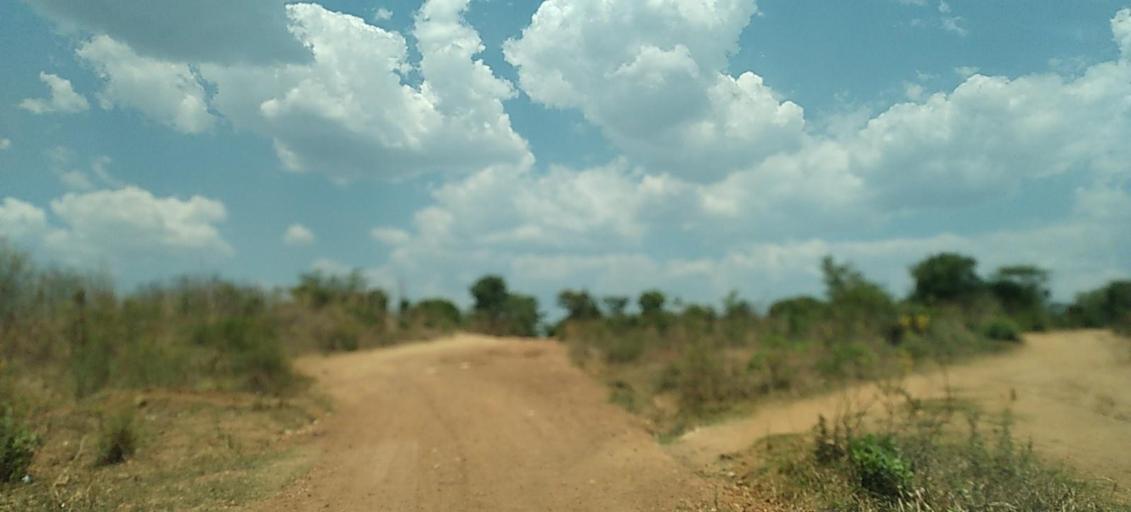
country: ZM
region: Copperbelt
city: Luanshya
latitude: -13.3723
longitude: 28.4191
